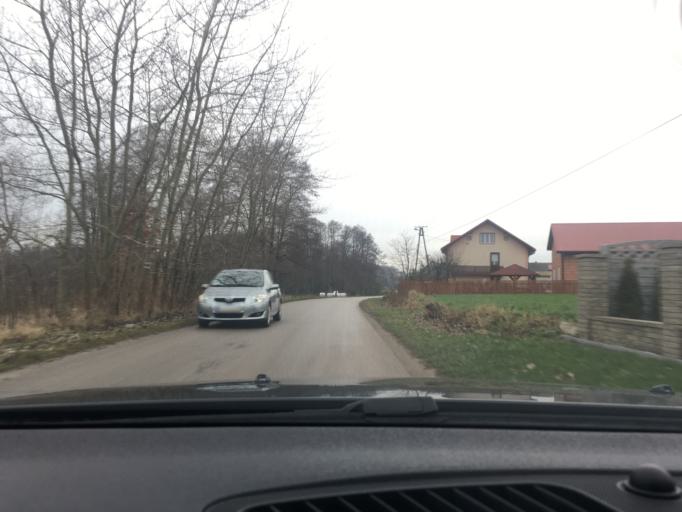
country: PL
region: Swietokrzyskie
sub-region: Powiat jedrzejowski
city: Imielno
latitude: 50.6423
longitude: 20.4011
